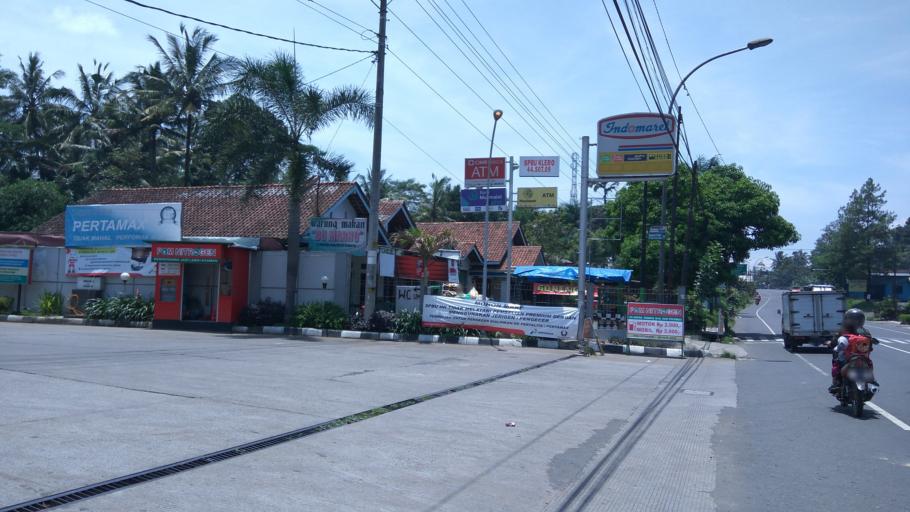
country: ID
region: Central Java
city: Salatiga
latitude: -7.3982
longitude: 110.5135
